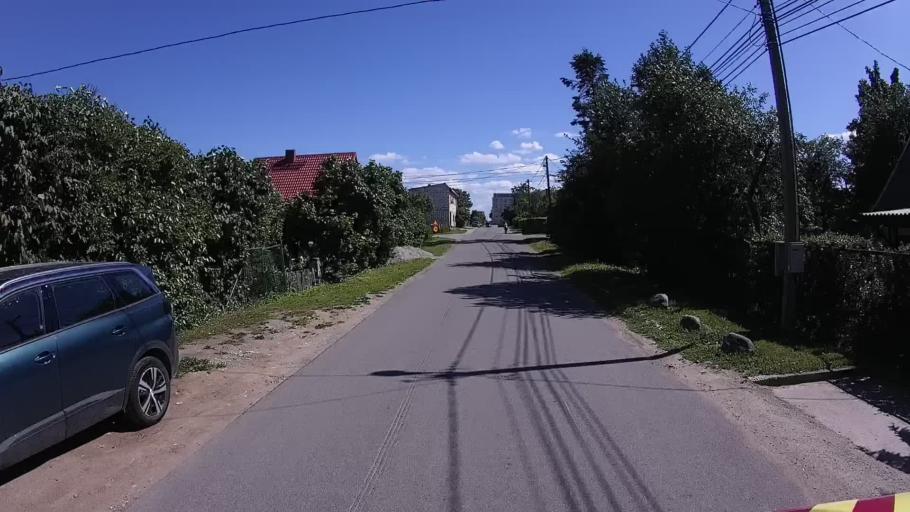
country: EE
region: Ida-Virumaa
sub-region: Kohtla-Jaerve linn
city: Kohtla-Jarve
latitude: 59.4079
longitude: 27.2940
